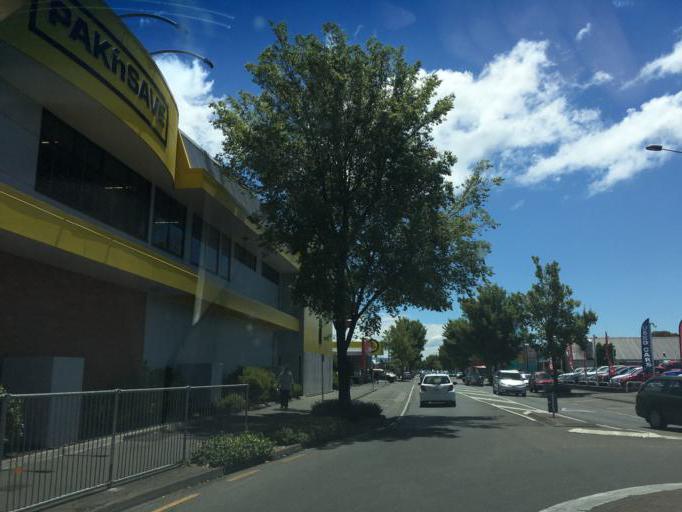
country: NZ
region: Hawke's Bay
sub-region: Hastings District
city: Hastings
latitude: -39.6366
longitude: 176.8375
